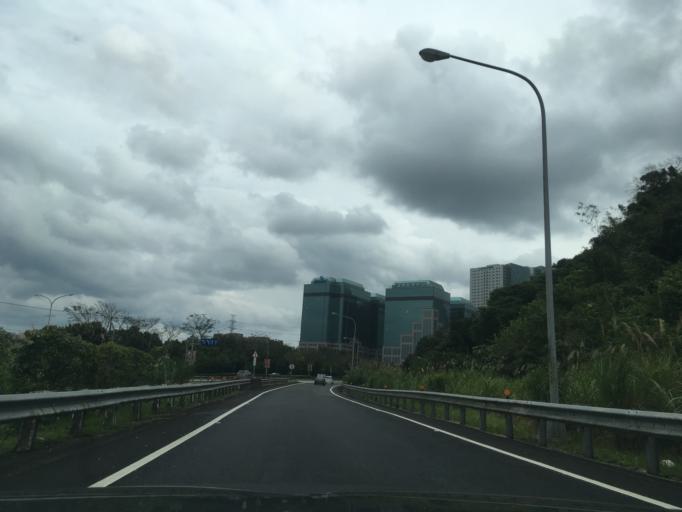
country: TW
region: Taipei
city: Taipei
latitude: 25.0570
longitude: 121.6419
